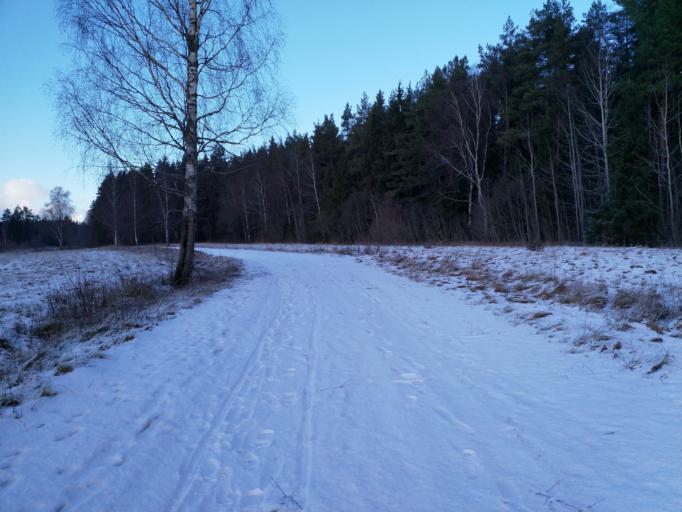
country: LV
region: Skrunda
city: Skrunda
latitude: 56.6747
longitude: 22.0838
